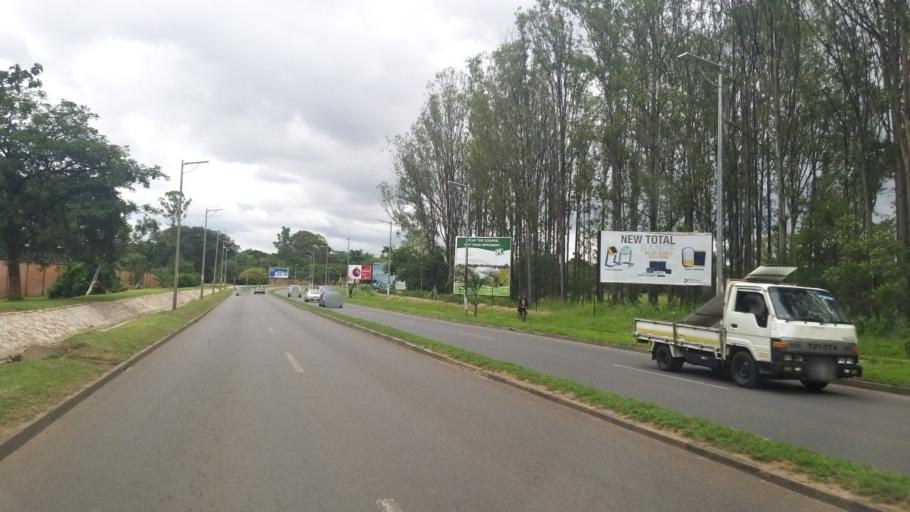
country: ZM
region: Lusaka
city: Lusaka
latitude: -15.4238
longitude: 28.3305
